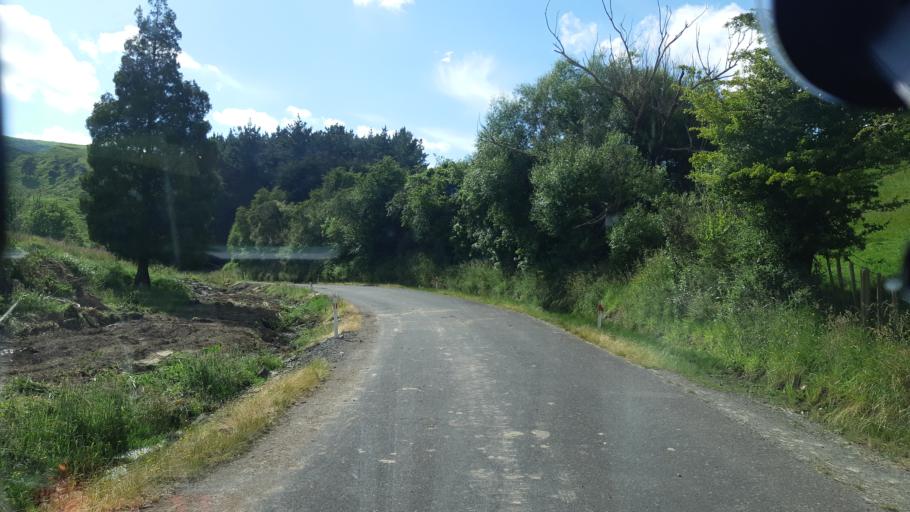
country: NZ
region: Manawatu-Wanganui
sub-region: Rangitikei District
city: Bulls
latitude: -39.9557
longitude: 175.5066
